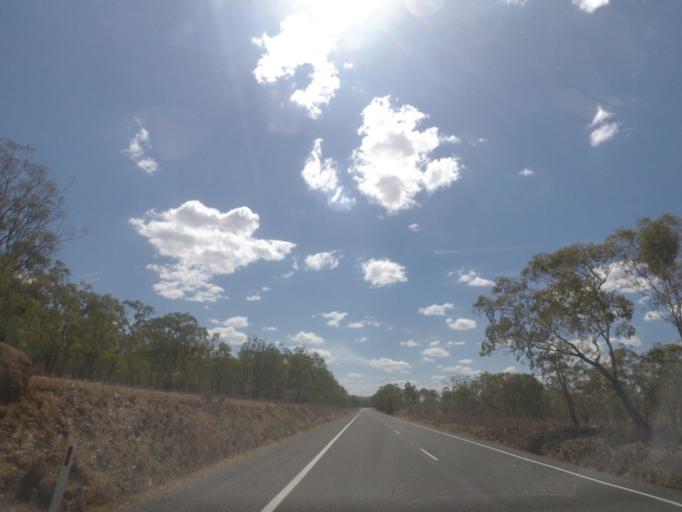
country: AU
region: Queensland
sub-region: Southern Downs
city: Warwick
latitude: -28.1638
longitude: 151.7146
